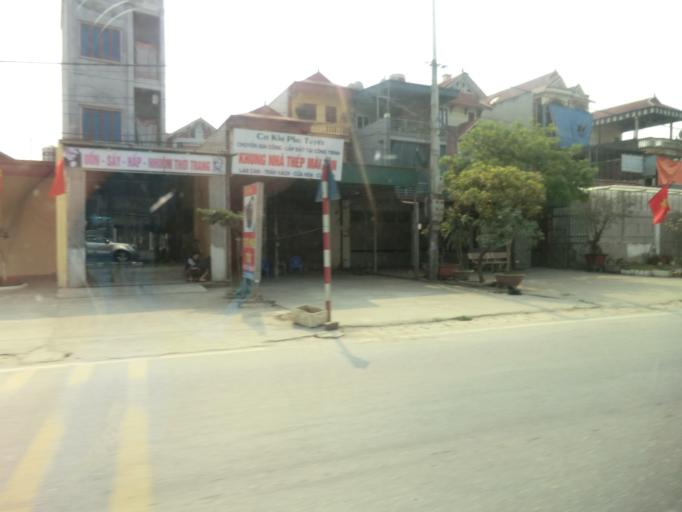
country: VN
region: Hoa Binh
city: Luong Son
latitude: 20.8576
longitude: 105.5848
